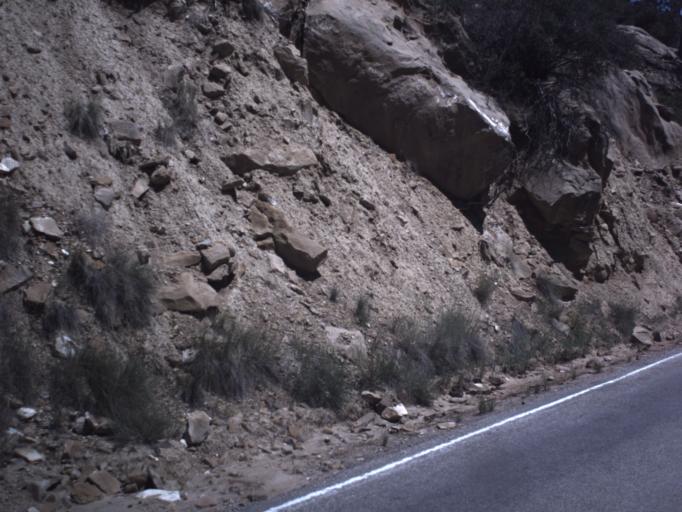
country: US
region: Utah
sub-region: Emery County
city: Orangeville
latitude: 39.2759
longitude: -111.2236
